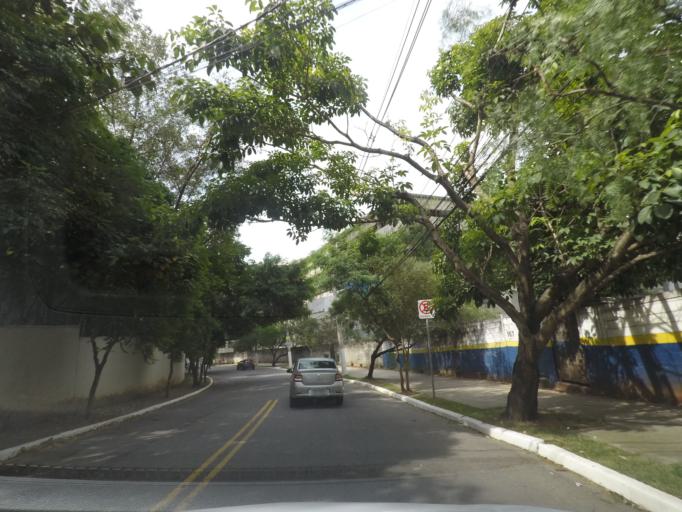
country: BR
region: Sao Paulo
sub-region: Taboao Da Serra
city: Taboao da Serra
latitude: -23.6315
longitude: -46.7390
